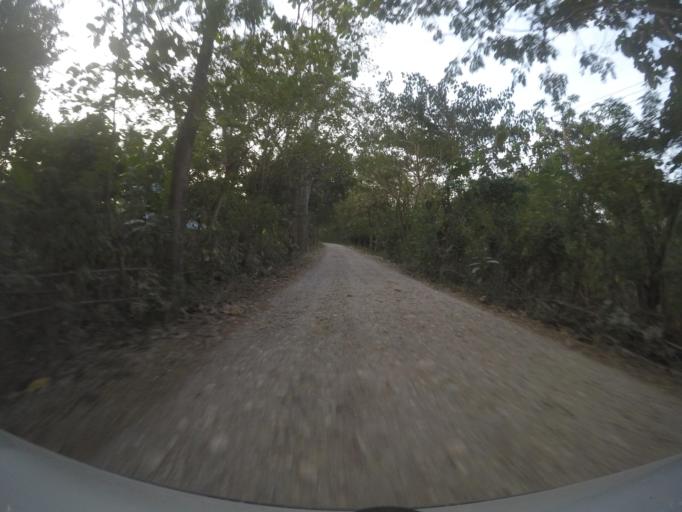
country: TL
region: Viqueque
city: Viqueque
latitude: -8.9343
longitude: 126.4127
